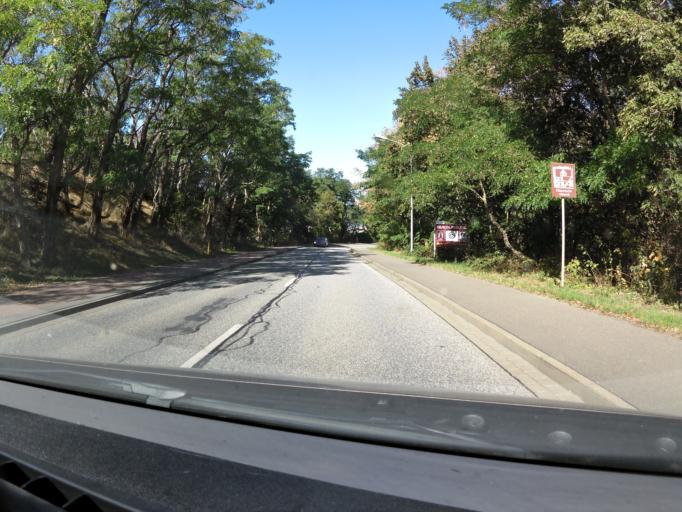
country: DE
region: Saxony-Anhalt
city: Quedlinburg
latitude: 51.7735
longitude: 11.1404
